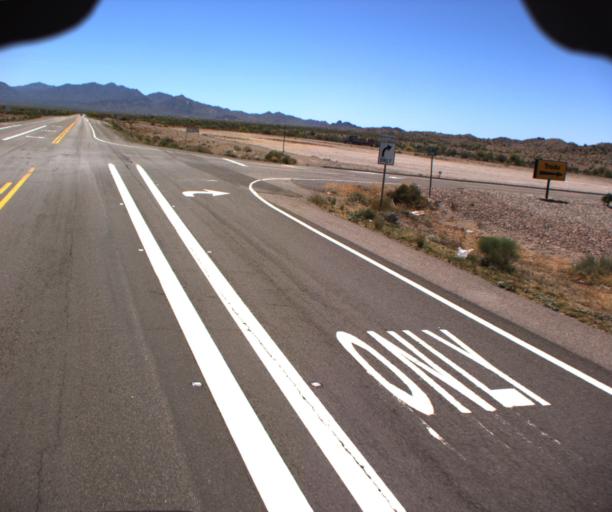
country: US
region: Arizona
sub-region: Mohave County
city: Desert Hills
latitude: 34.7232
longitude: -114.3139
